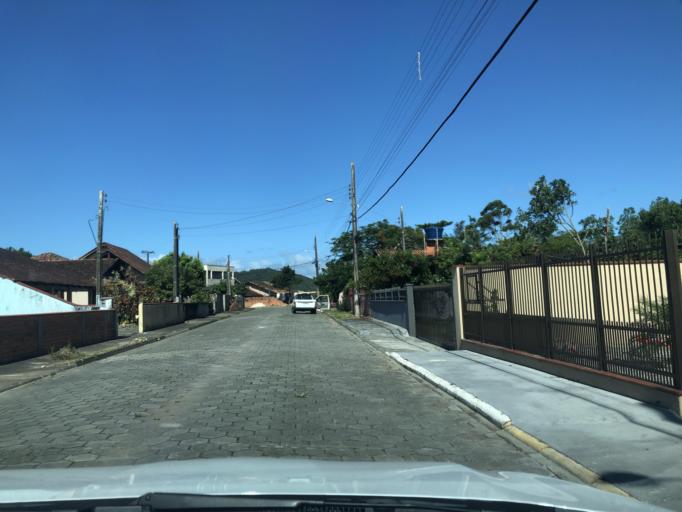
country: BR
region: Santa Catarina
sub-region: Sao Francisco Do Sul
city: Sao Francisco do Sul
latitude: -26.2292
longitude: -48.5181
